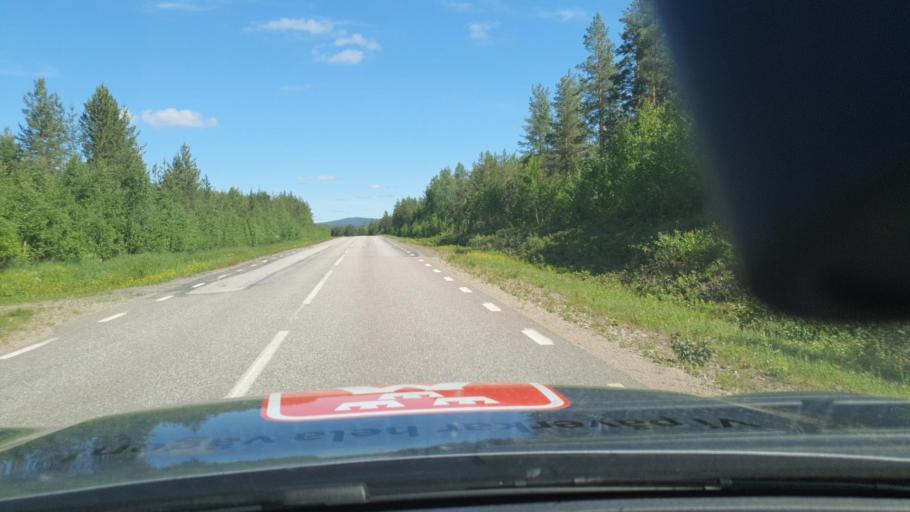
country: SE
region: Norrbotten
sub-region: Overkalix Kommun
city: OEverkalix
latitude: 66.7391
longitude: 22.6699
